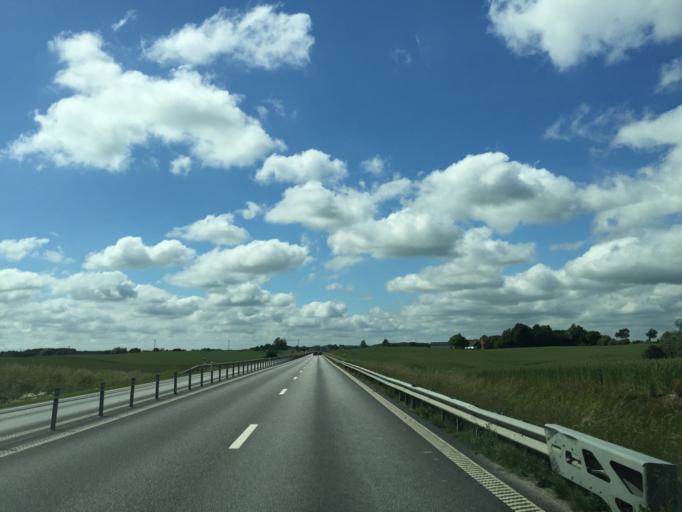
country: SE
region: Skane
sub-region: Skurups Kommun
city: Rydsgard
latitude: 55.4859
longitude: 13.5655
